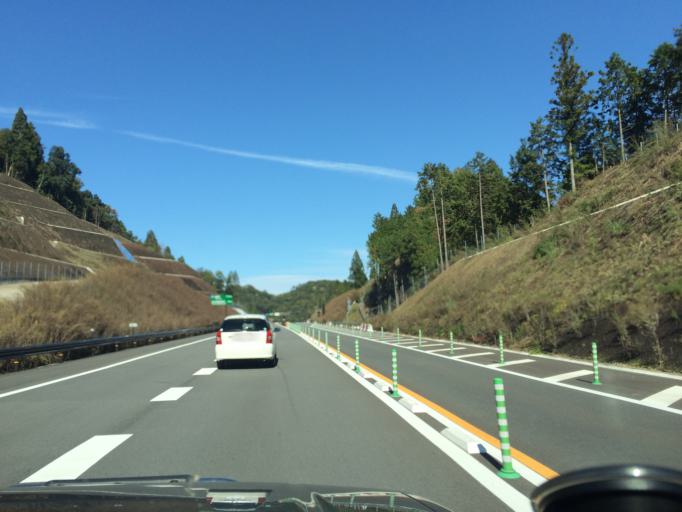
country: JP
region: Hyogo
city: Toyooka
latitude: 35.4272
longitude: 134.7668
